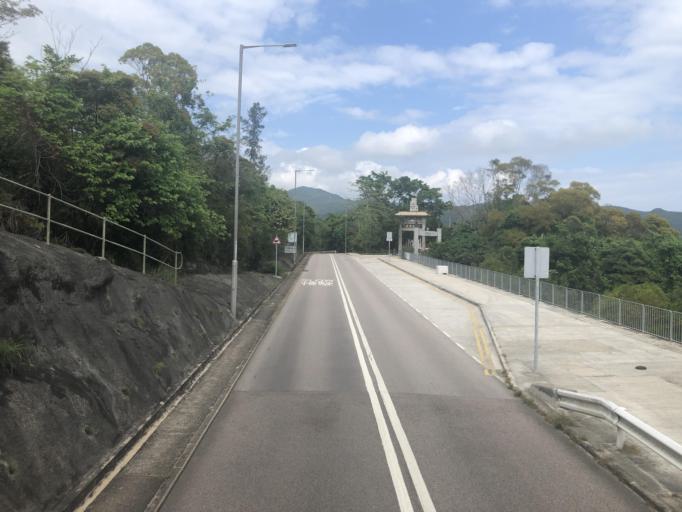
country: HK
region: Sai Kung
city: Sai Kung
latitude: 22.3867
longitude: 114.3055
